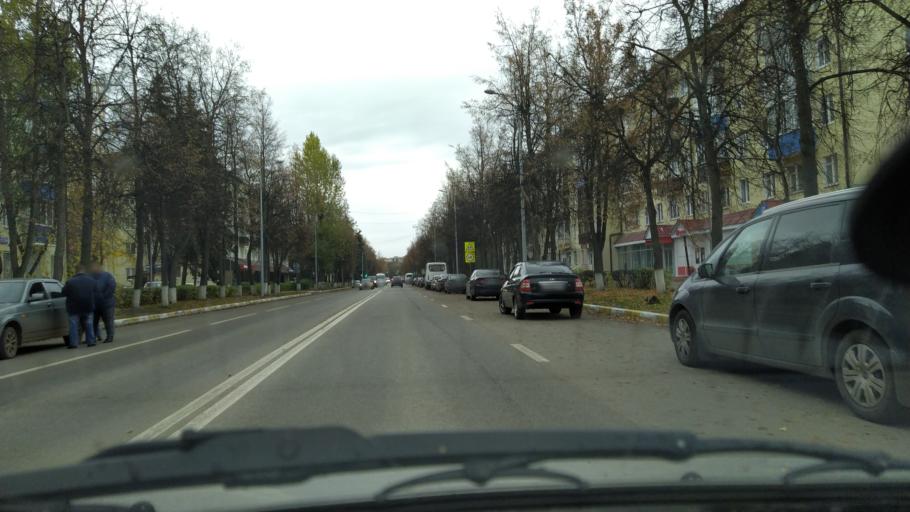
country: RU
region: Moskovskaya
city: Voskresensk
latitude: 55.3249
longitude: 38.6594
